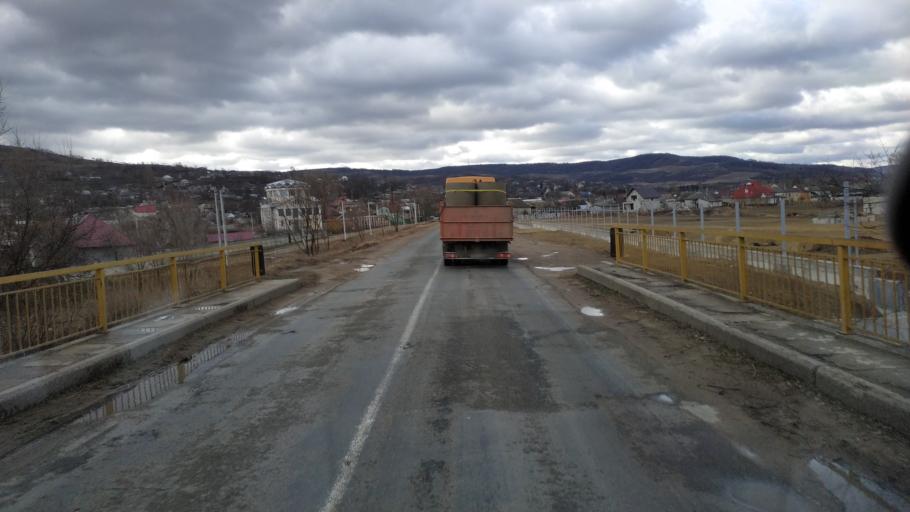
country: MD
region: Stinga Nistrului
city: Bucovat
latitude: 47.1627
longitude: 28.4351
